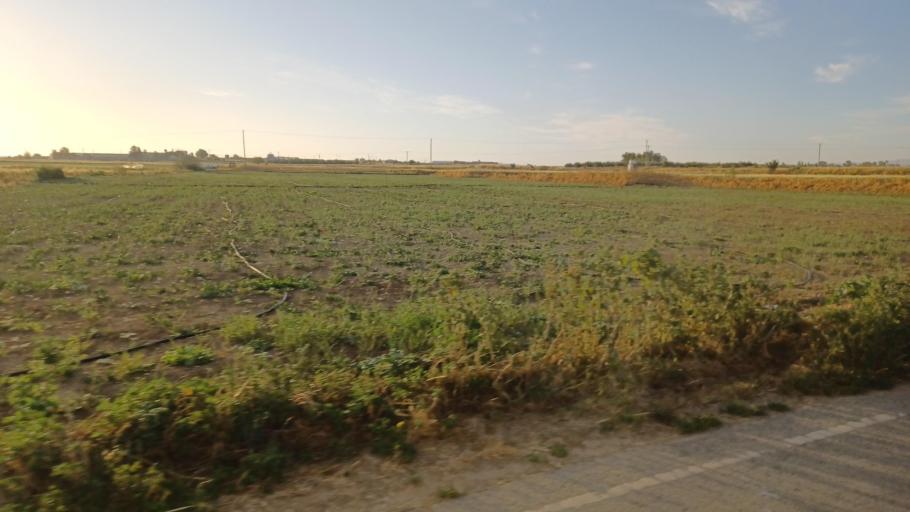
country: CY
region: Lefkosia
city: Akaki
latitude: 35.1583
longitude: 33.1349
